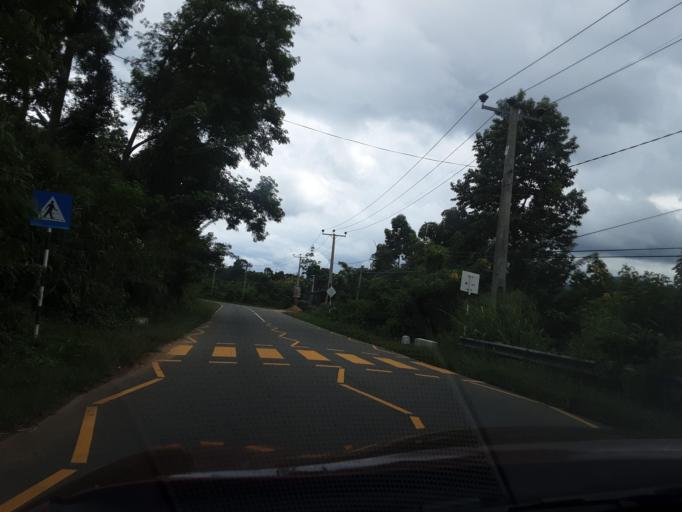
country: LK
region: Uva
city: Monaragala
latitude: 6.9102
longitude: 81.2117
